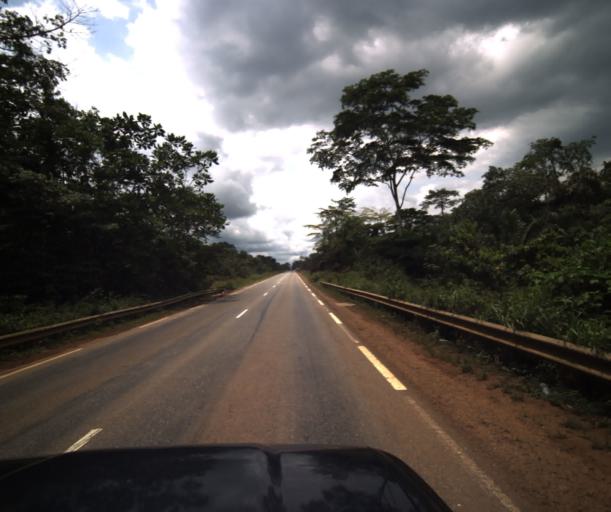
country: CM
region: Centre
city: Eseka
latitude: 3.8777
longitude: 10.6818
